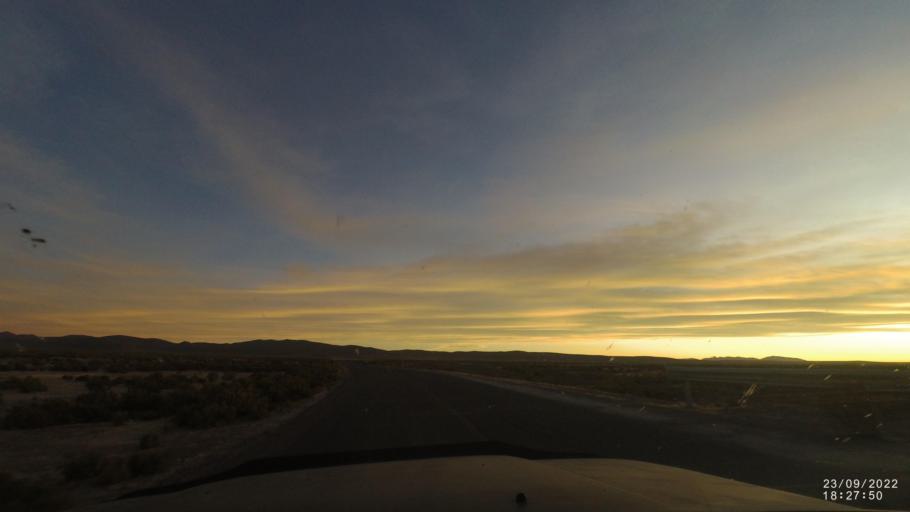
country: BO
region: Oruro
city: Challapata
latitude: -19.3315
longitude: -67.1723
